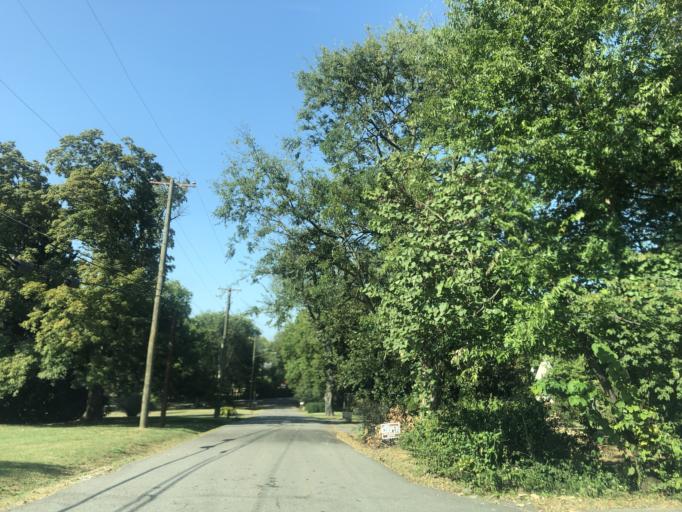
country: US
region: Tennessee
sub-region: Davidson County
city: Oak Hill
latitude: 36.1121
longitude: -86.8134
